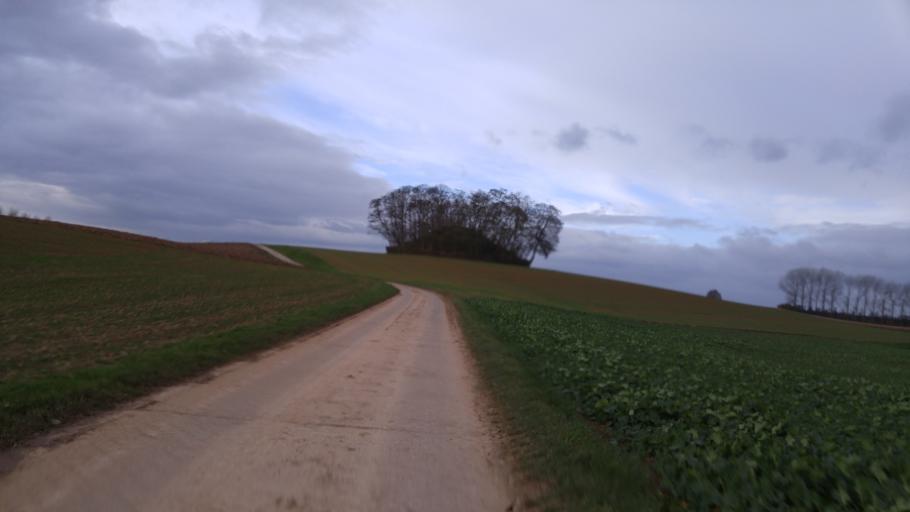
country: BE
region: Wallonia
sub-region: Province du Brabant Wallon
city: Ramillies
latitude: 50.6222
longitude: 4.8941
